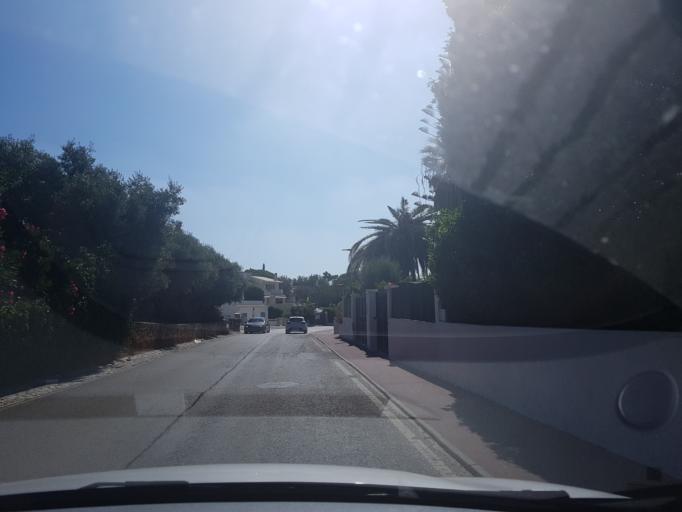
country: PT
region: Faro
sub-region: Lagoa
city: Carvoeiro
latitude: 37.0950
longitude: -8.4622
